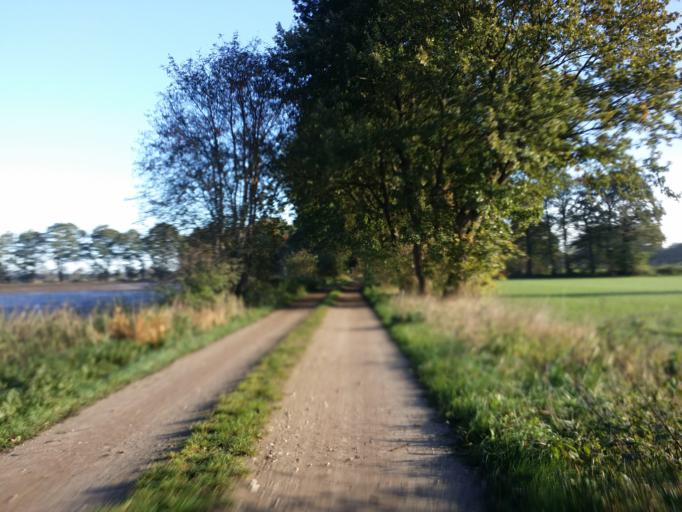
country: DE
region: Lower Saxony
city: Tarmstedt
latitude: 53.1984
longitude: 9.0543
